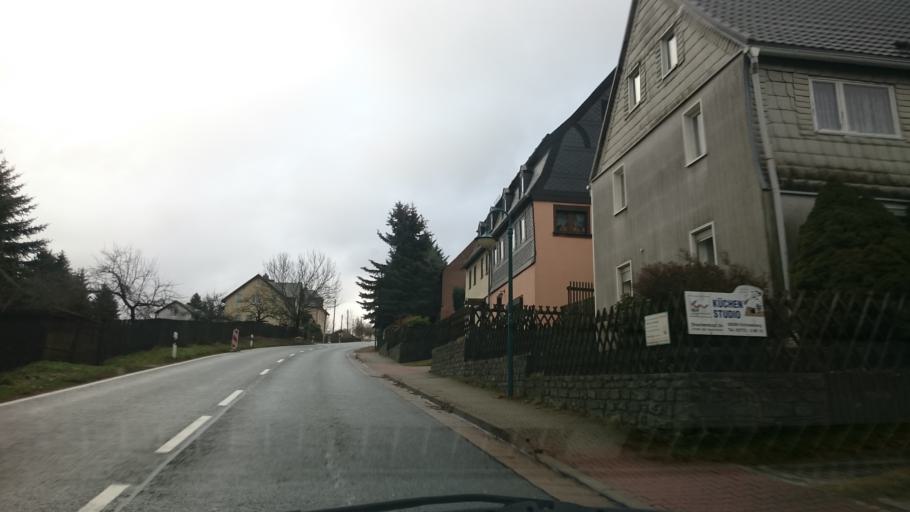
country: DE
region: Saxony
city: Wildenfels
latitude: 50.6149
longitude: 12.5838
